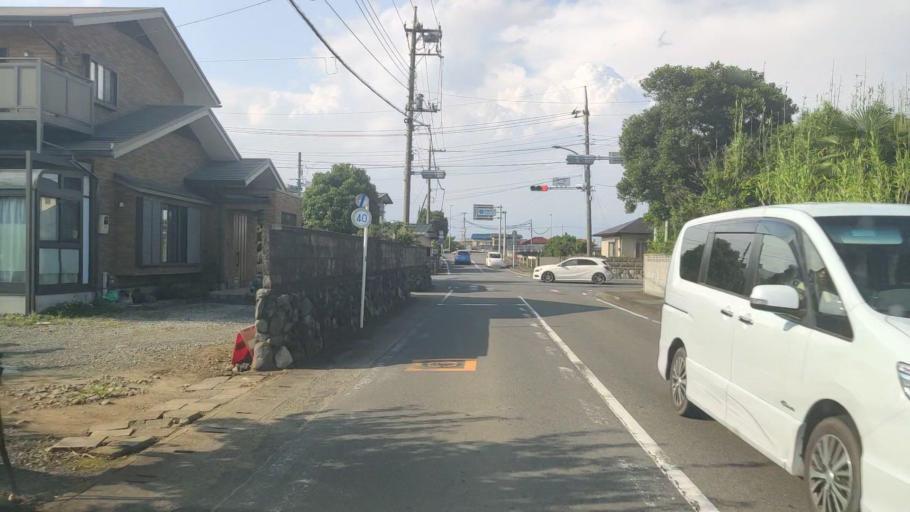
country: JP
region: Kanagawa
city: Isehara
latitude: 35.3826
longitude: 139.3386
